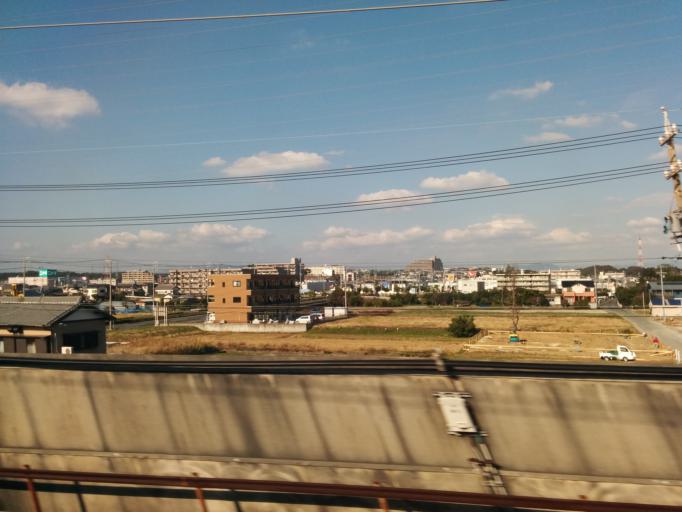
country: JP
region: Shizuoka
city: Hamamatsu
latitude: 34.6943
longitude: 137.6803
